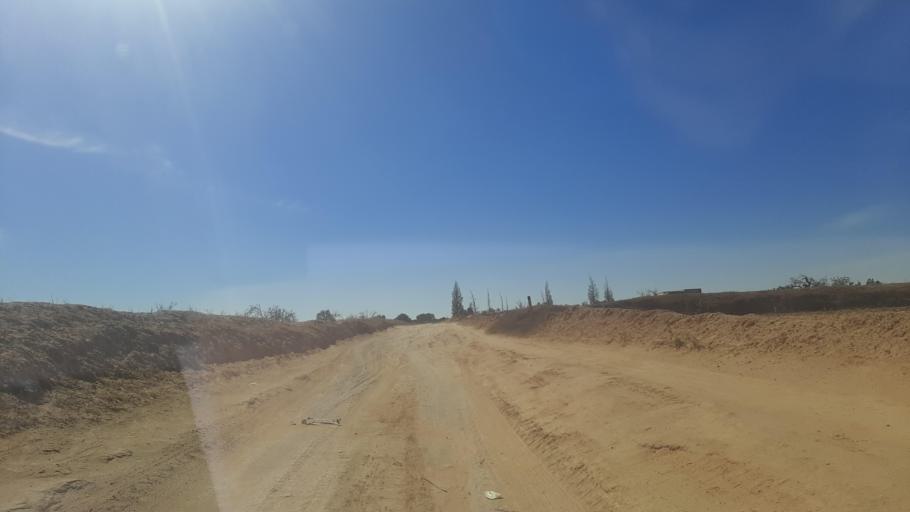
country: TN
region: Safaqis
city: Sfax
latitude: 34.8501
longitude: 10.5622
